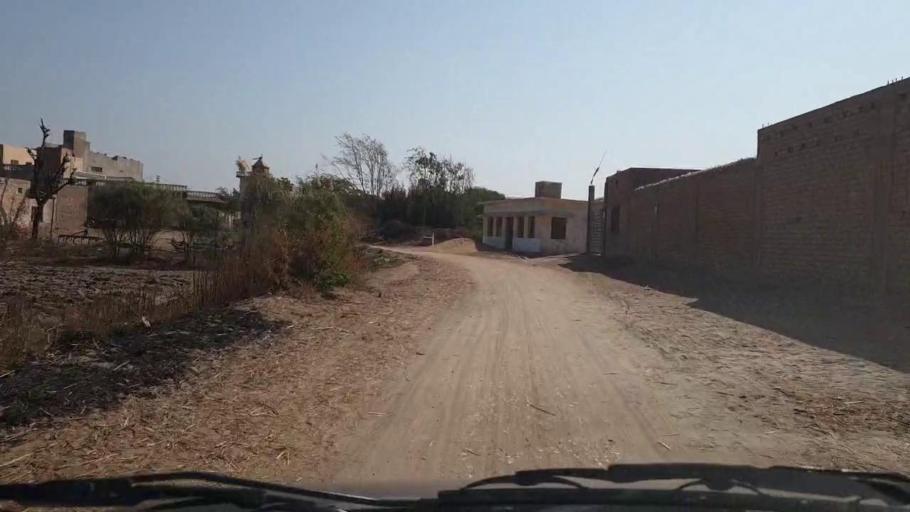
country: PK
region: Sindh
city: Samaro
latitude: 25.2699
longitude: 69.2519
